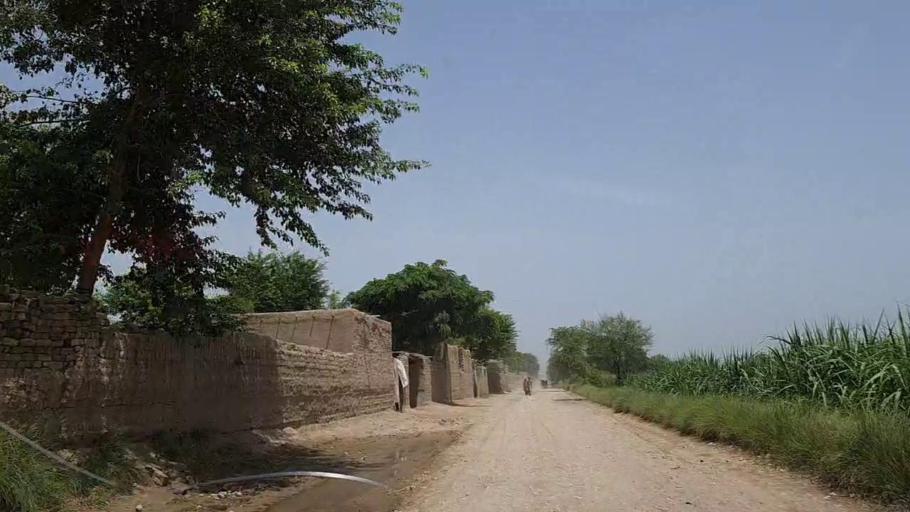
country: PK
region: Sindh
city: Tharu Shah
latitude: 26.9029
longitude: 68.0067
